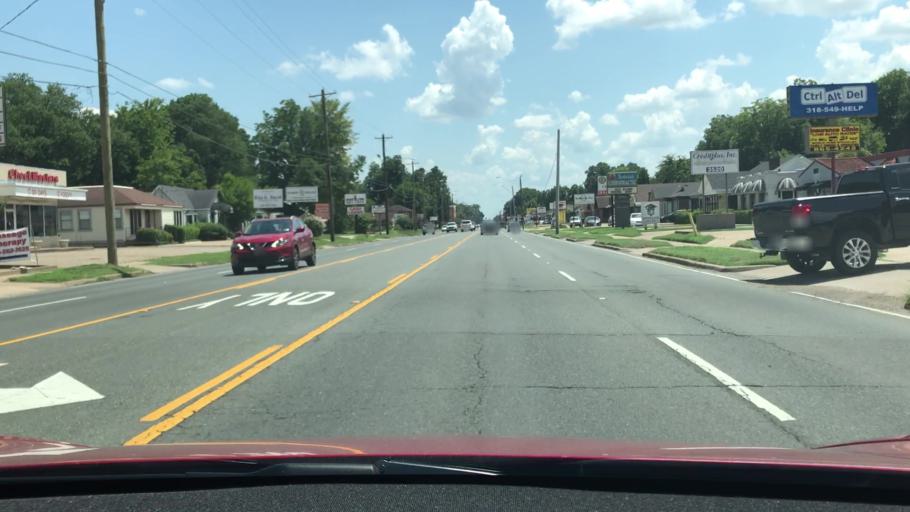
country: US
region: Louisiana
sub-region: Bossier Parish
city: Bossier City
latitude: 32.4761
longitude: -93.7222
